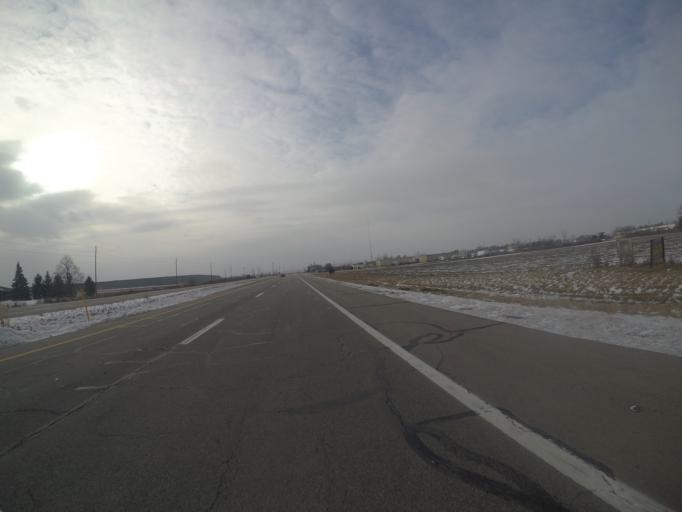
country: US
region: Ohio
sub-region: Wood County
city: Walbridge
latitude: 41.5641
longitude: -83.5197
